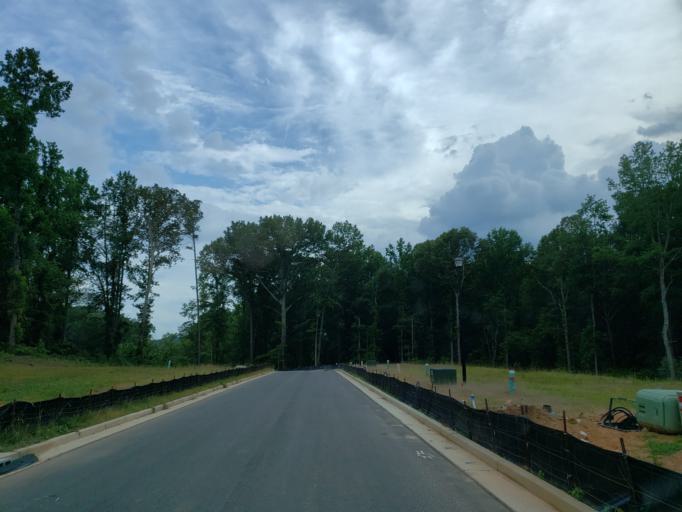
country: US
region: Georgia
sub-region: Cherokee County
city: Holly Springs
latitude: 34.1783
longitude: -84.4351
